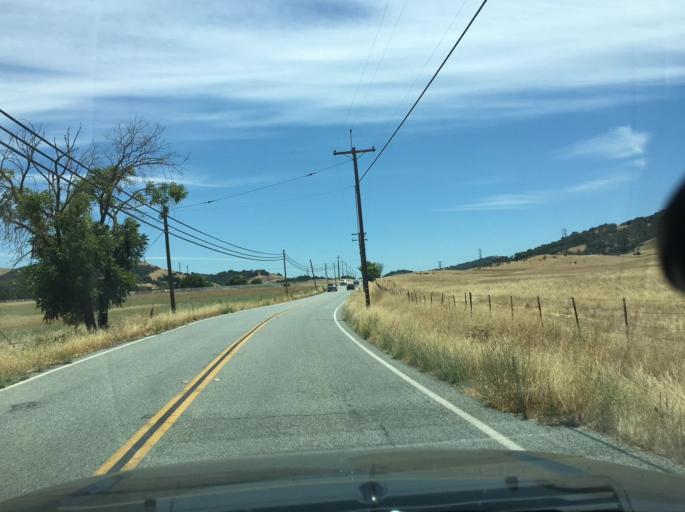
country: US
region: California
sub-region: Santa Clara County
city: Seven Trees
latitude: 37.1967
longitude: -121.8129
